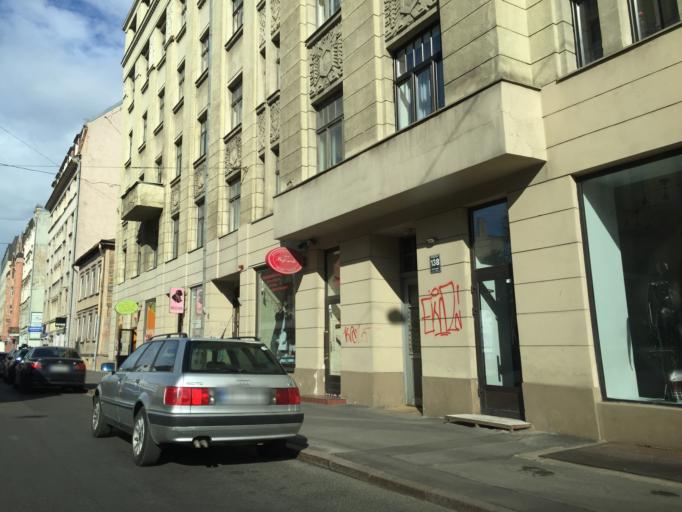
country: LV
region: Riga
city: Riga
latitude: 56.9637
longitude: 24.1389
